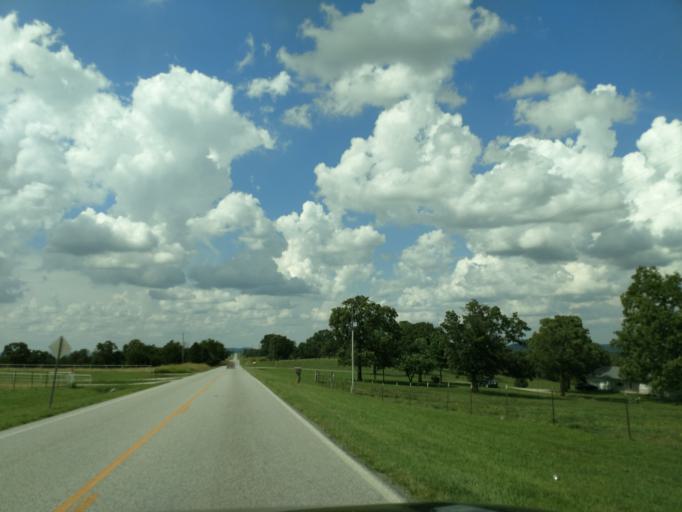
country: US
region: Arkansas
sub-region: Carroll County
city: Berryville
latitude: 36.4380
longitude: -93.5562
